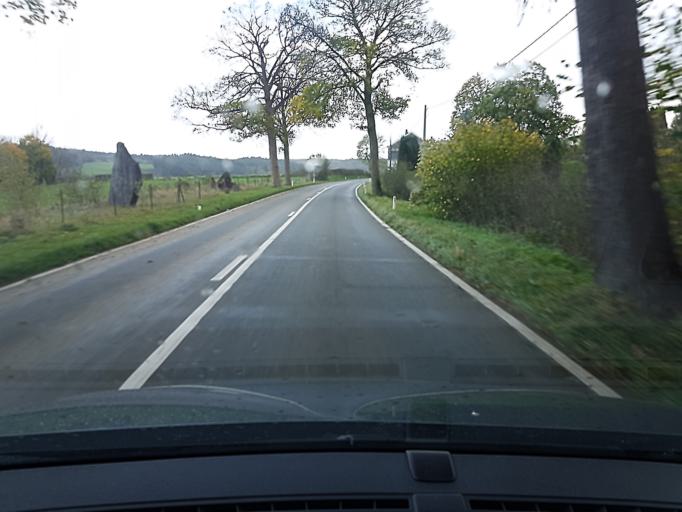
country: BE
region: Wallonia
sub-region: Province de Liege
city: Trooz
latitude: 50.5193
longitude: 5.7278
